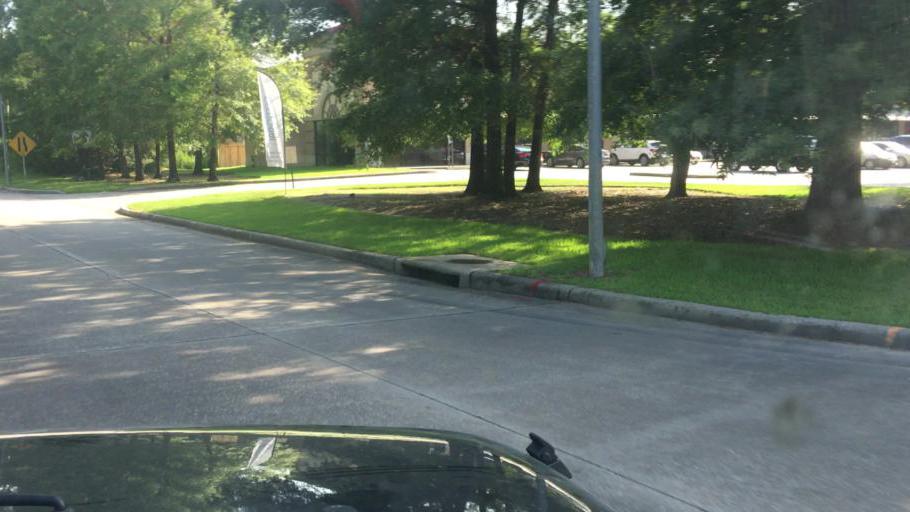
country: US
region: Texas
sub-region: Harris County
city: Atascocita
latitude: 30.0082
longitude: -95.1724
